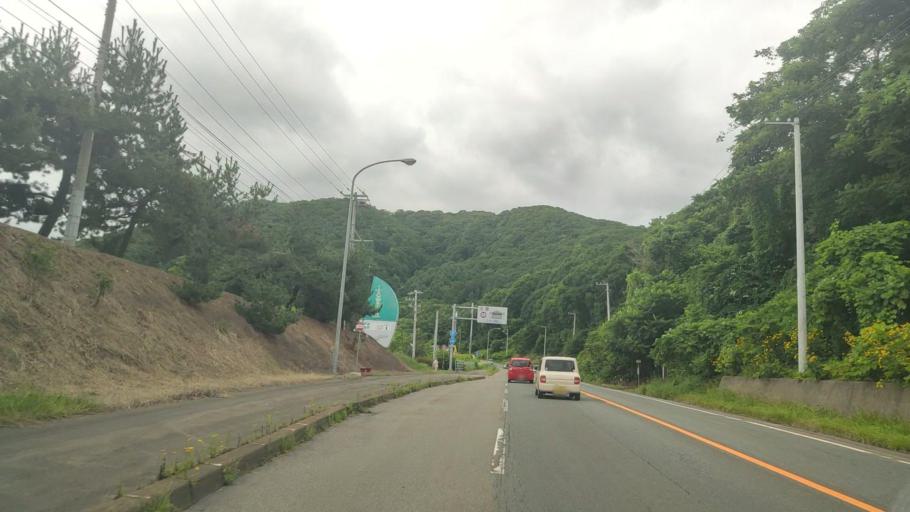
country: JP
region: Hokkaido
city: Date
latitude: 42.5595
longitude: 140.7462
